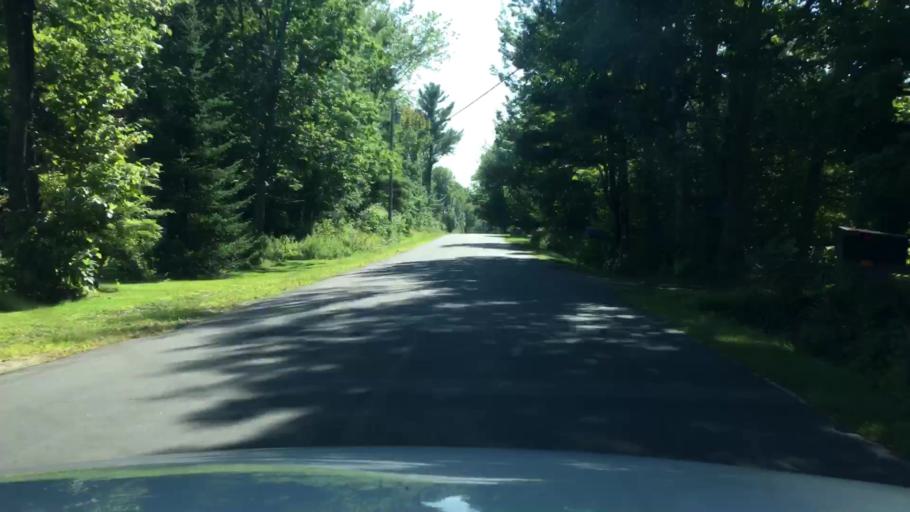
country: US
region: Maine
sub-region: Kennebec County
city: Monmouth
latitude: 44.2620
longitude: -70.0544
